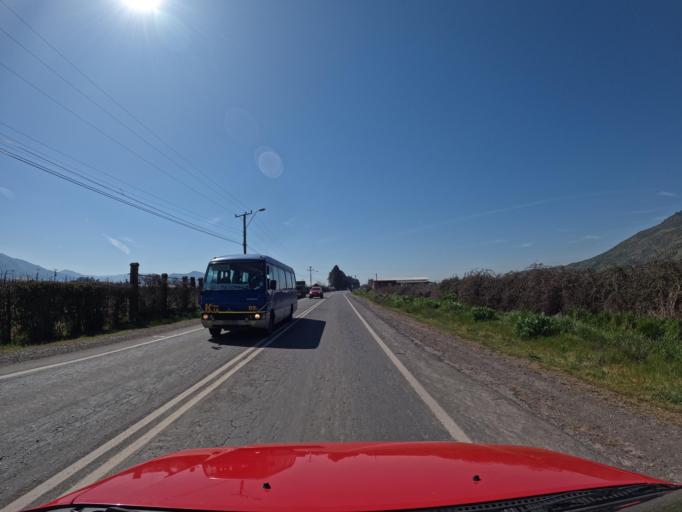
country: CL
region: Maule
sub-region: Provincia de Curico
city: Rauco
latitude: -35.0104
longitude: -71.4149
